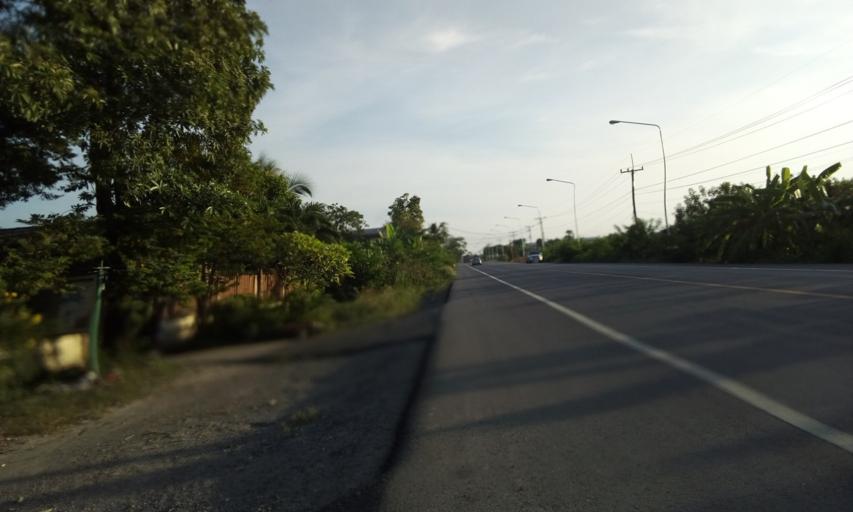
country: TH
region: Pathum Thani
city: Ban Rangsit
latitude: 14.0371
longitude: 100.8440
